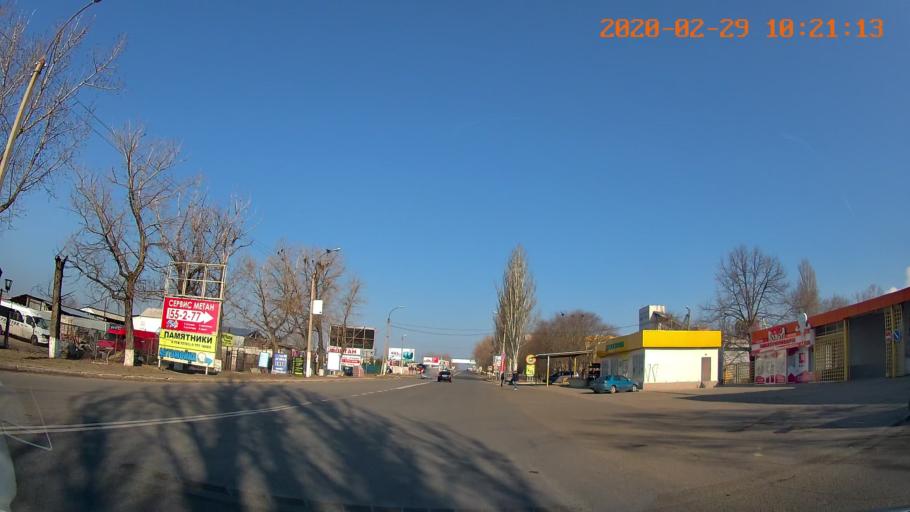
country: MD
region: Telenesti
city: Tiraspolul Nou
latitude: 46.8647
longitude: 29.6096
